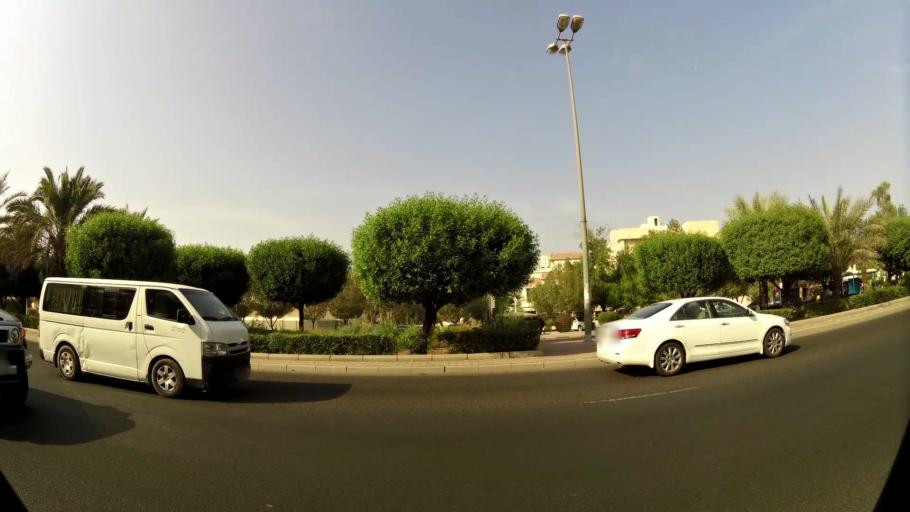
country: KW
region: Al Asimah
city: Ash Shamiyah
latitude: 29.3328
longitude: 47.9794
